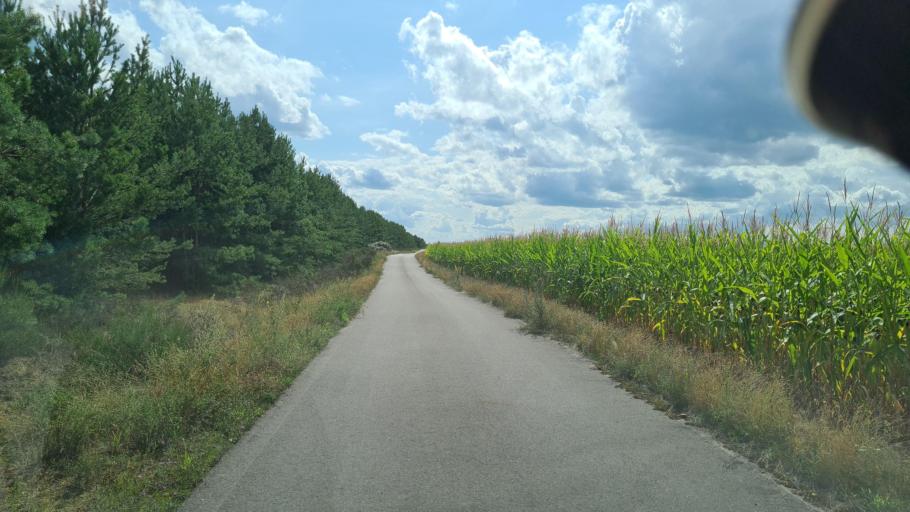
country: DE
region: Brandenburg
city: Drebkau
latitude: 51.6020
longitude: 14.2902
